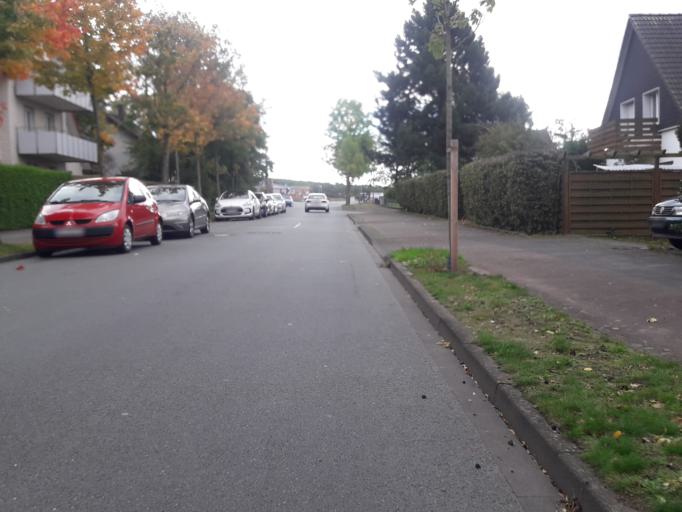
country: DE
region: North Rhine-Westphalia
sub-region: Regierungsbezirk Detmold
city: Paderborn
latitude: 51.7204
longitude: 8.8089
